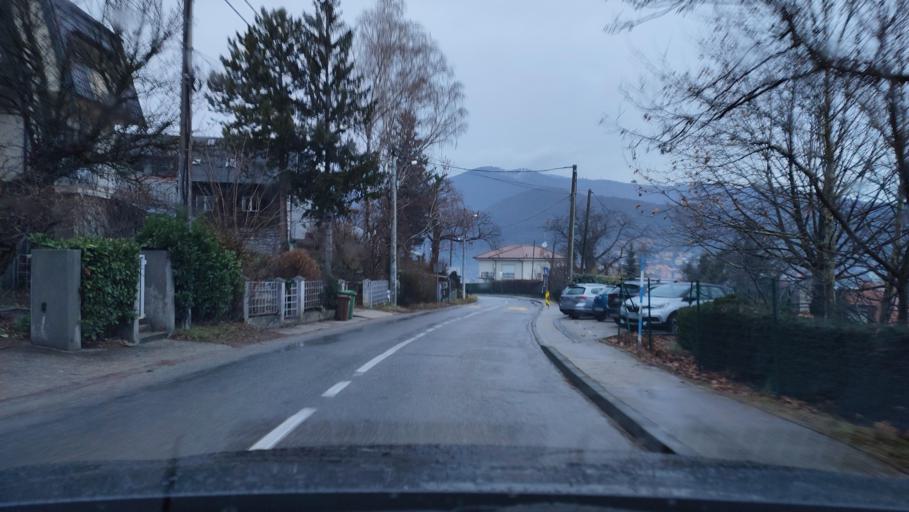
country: HR
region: Grad Zagreb
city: Zagreb
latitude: 45.8491
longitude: 15.9535
